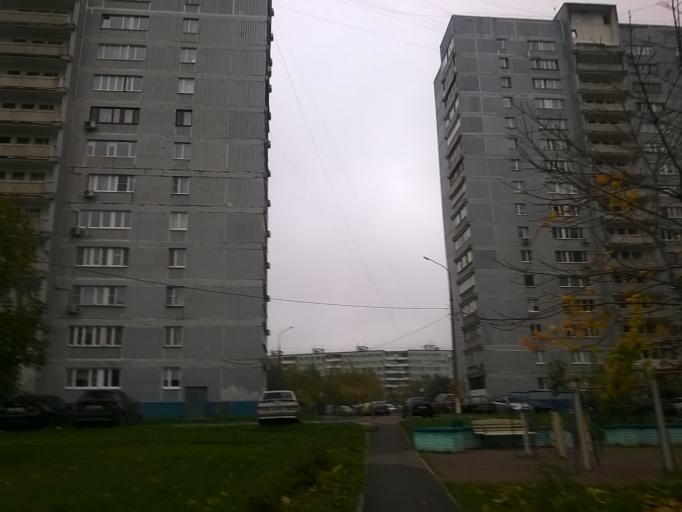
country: RU
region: Moscow
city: Tyoply Stan
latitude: 55.6312
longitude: 37.4803
